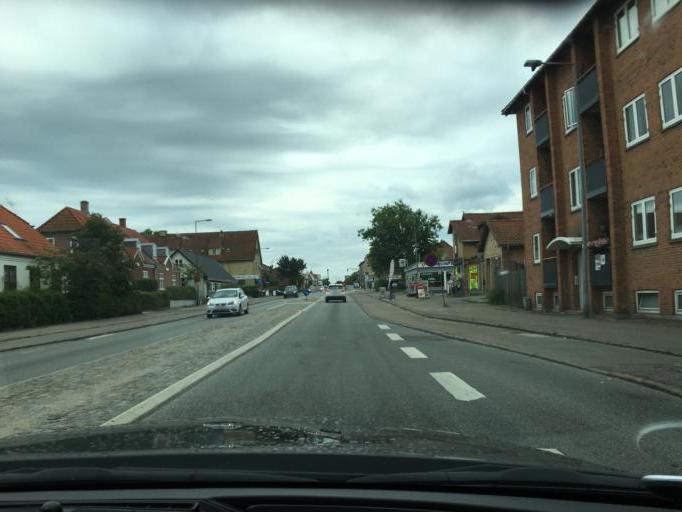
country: DK
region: Capital Region
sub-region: Horsholm Kommune
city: Horsholm
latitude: 55.8863
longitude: 12.4973
